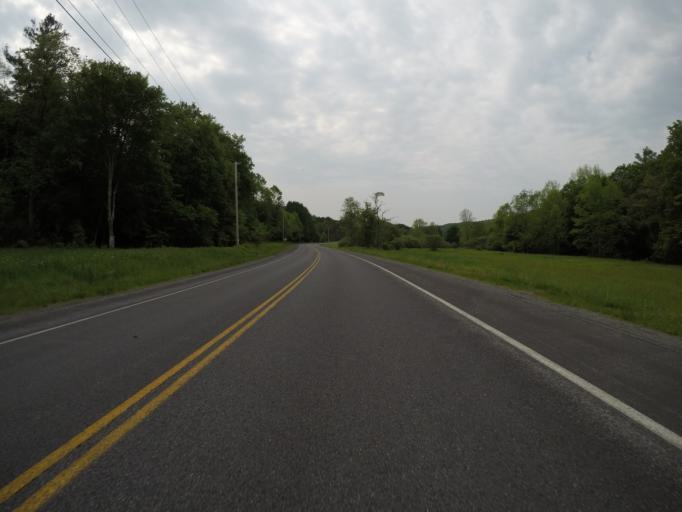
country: US
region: New York
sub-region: Sullivan County
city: Livingston Manor
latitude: 41.9974
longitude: -74.8937
